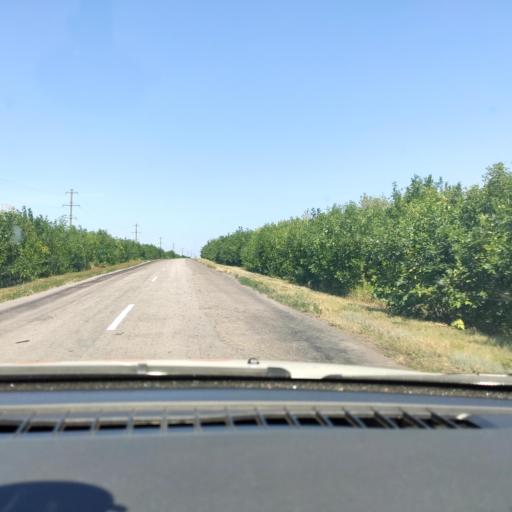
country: RU
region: Voronezj
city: Ol'khovatka
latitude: 50.5894
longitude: 39.2872
